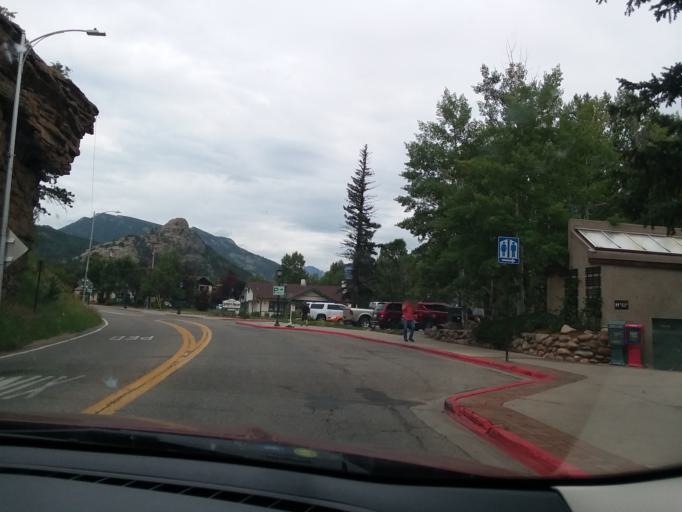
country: US
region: Colorado
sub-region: Larimer County
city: Estes Park
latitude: 40.3764
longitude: -105.5266
